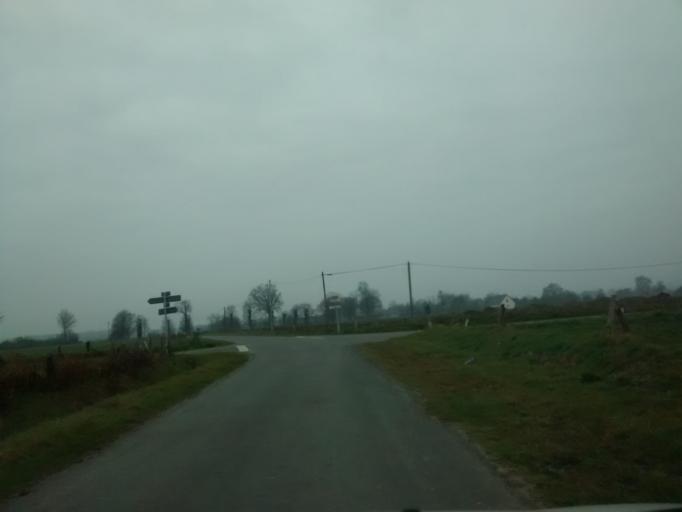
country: FR
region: Brittany
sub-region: Departement d'Ille-et-Vilaine
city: Sens-de-Bretagne
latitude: 48.3792
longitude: -1.5326
